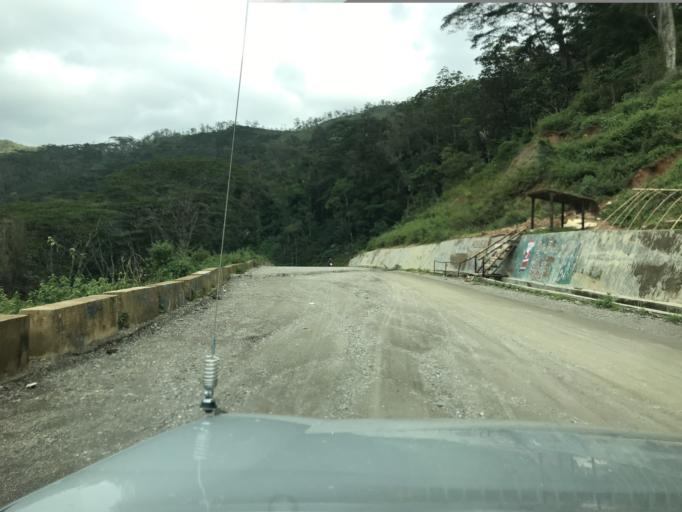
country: TL
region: Aileu
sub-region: Aileu Villa
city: Aileu
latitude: -8.6728
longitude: 125.5505
